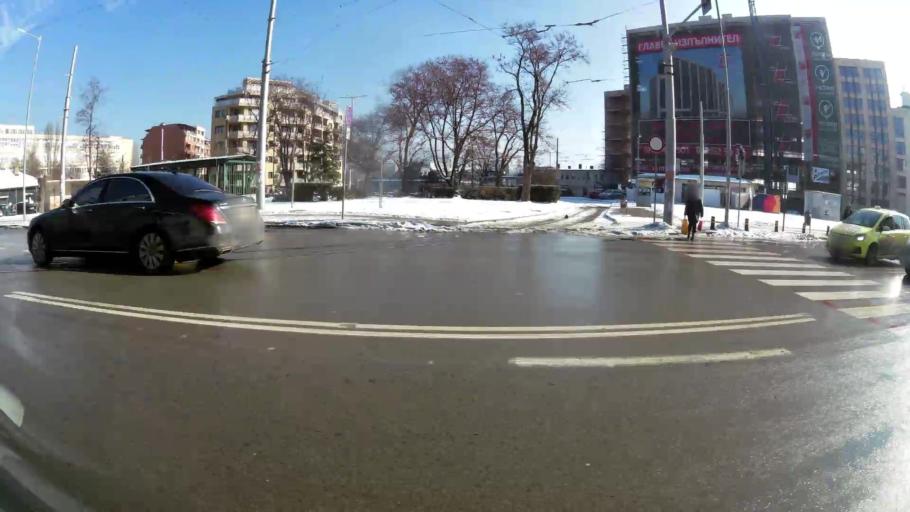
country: BG
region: Sofia-Capital
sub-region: Stolichna Obshtina
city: Sofia
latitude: 42.6602
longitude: 23.3166
